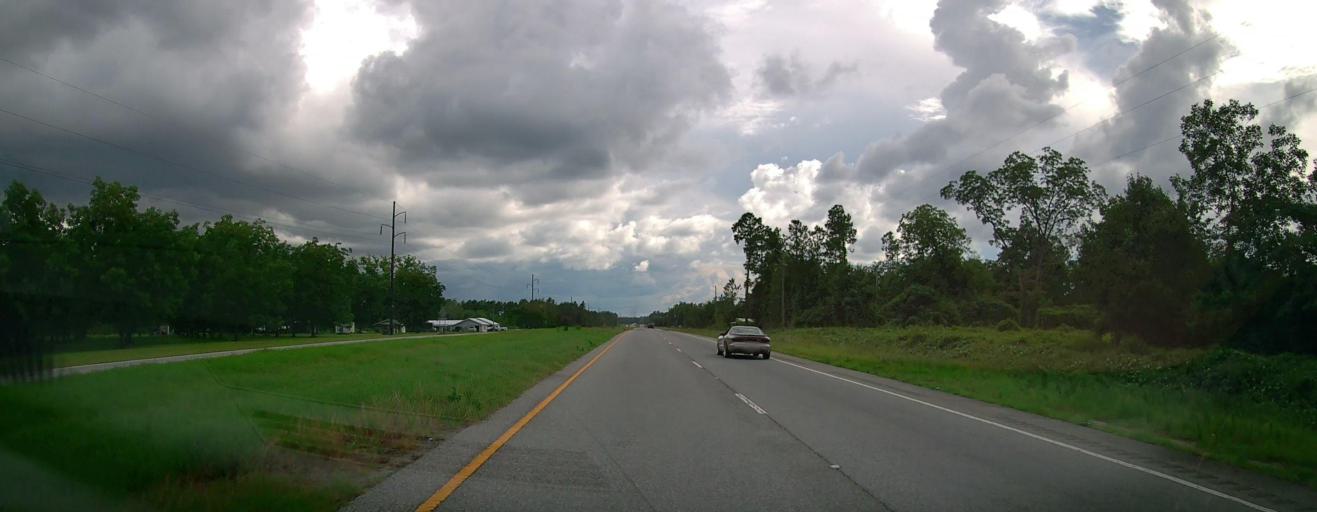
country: US
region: Georgia
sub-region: Pierce County
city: Blackshear
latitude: 31.4302
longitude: -82.0917
